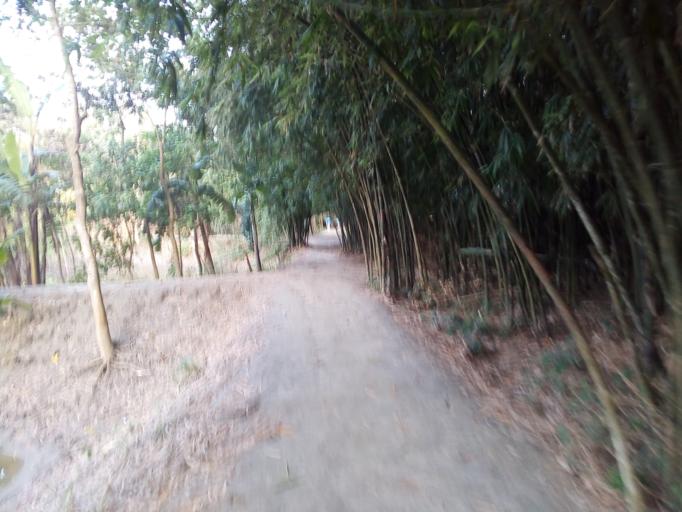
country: BD
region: Rangpur Division
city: Nageswari
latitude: 25.8692
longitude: 89.7847
